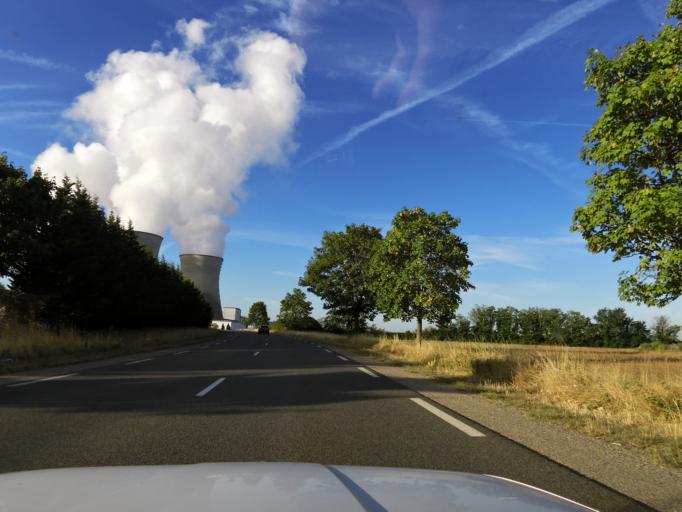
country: FR
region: Rhone-Alpes
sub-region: Departement de l'Isere
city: Hieres-sur-Amby
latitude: 45.8097
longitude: 5.2700
